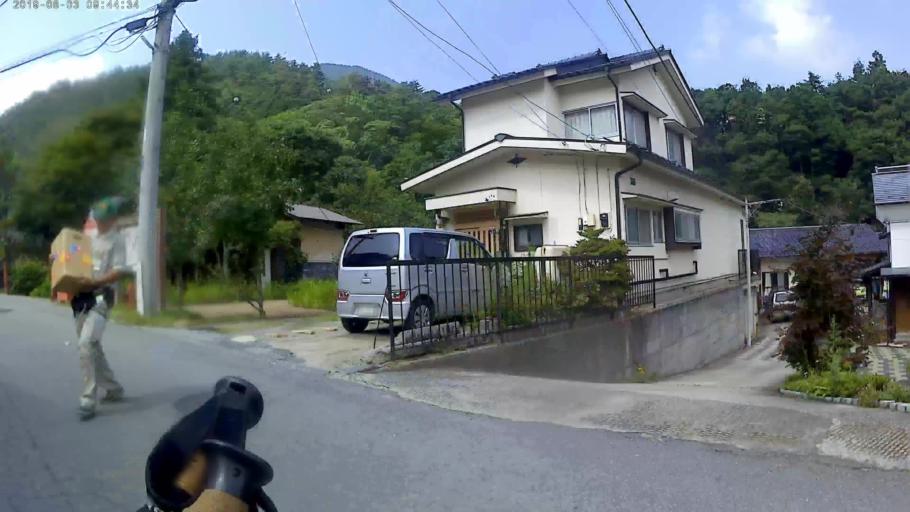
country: JP
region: Yamanashi
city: Enzan
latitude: 35.6362
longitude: 138.7695
